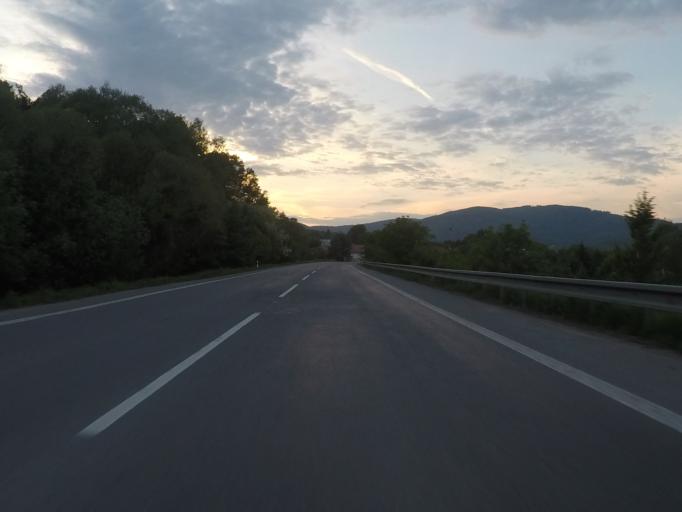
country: SK
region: Banskobystricky
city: Rimavska Sobota
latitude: 48.4978
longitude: 19.9371
